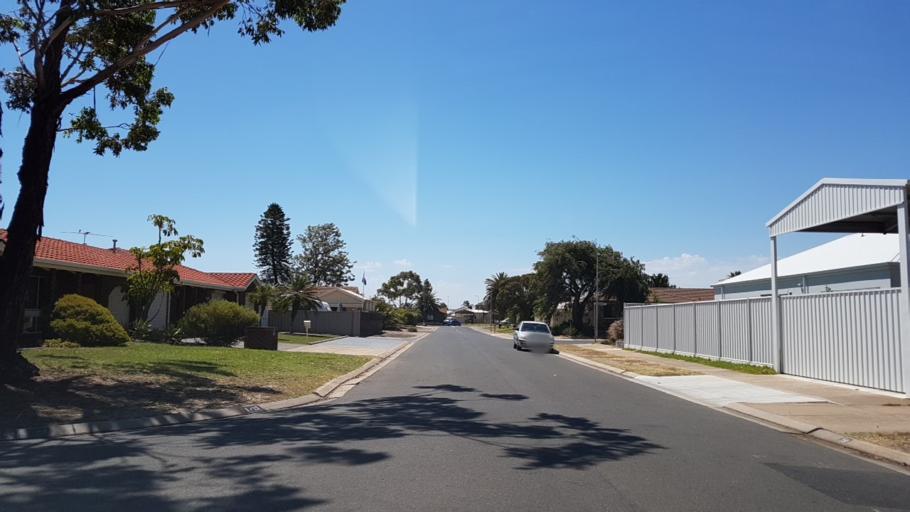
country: AU
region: South Australia
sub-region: Port Adelaide Enfield
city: Birkenhead
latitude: -34.7948
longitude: 138.4956
